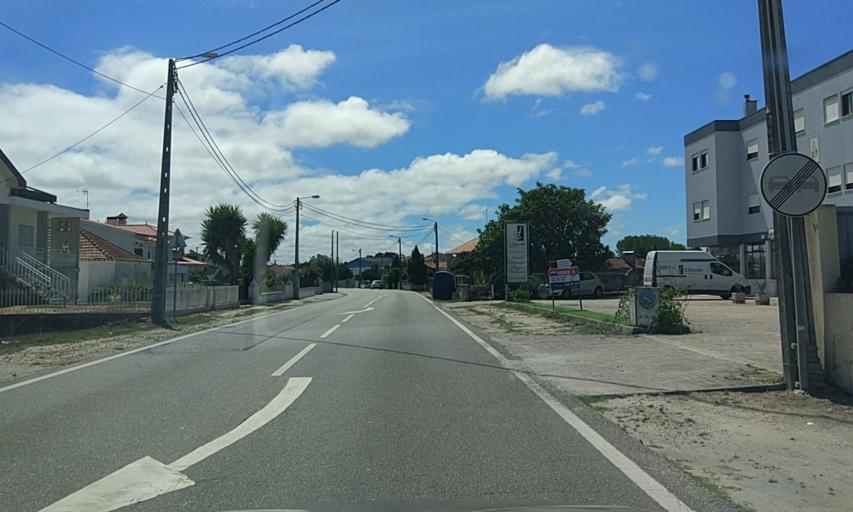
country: PT
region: Aveiro
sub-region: Vagos
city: Vagos
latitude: 40.5296
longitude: -8.6790
